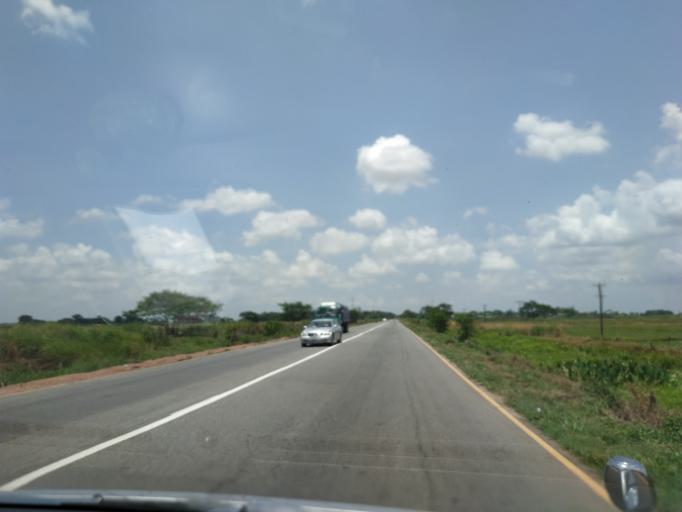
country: MM
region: Bago
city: Thanatpin
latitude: 17.4532
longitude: 96.6138
